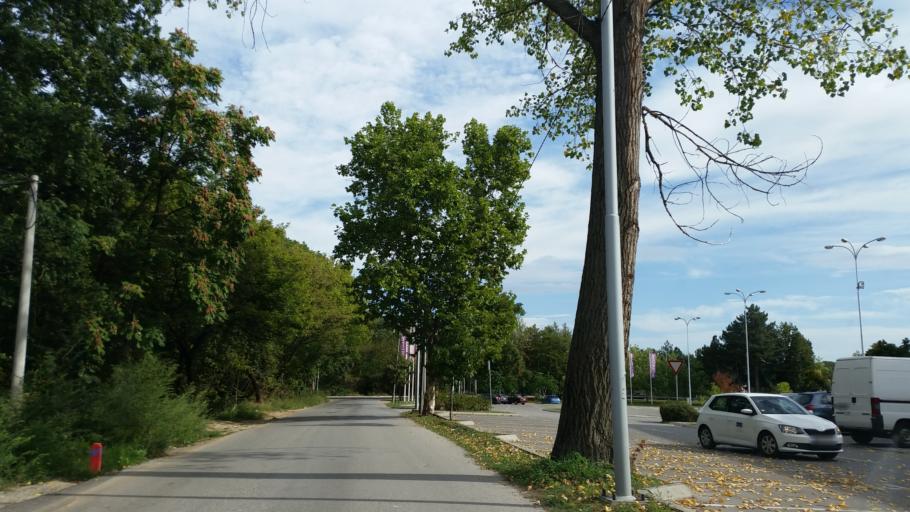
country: RS
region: Central Serbia
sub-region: Belgrade
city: Zemun
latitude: 44.8251
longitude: 20.3874
